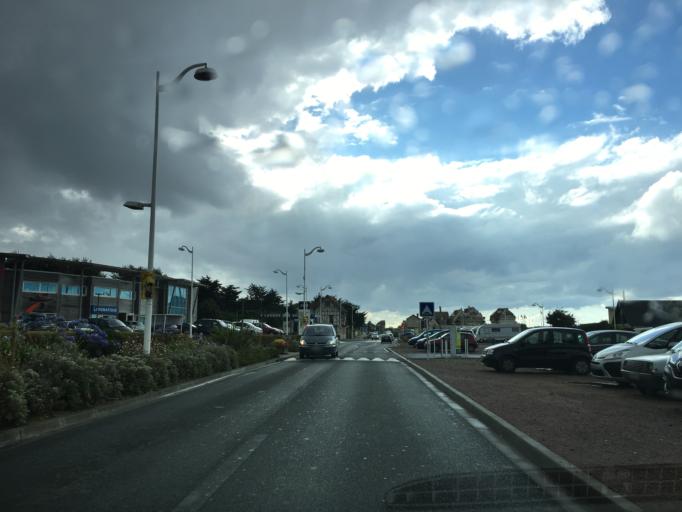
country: FR
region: Lower Normandy
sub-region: Departement du Calvados
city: Bernieres-sur-Mer
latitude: 49.3347
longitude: -0.4180
